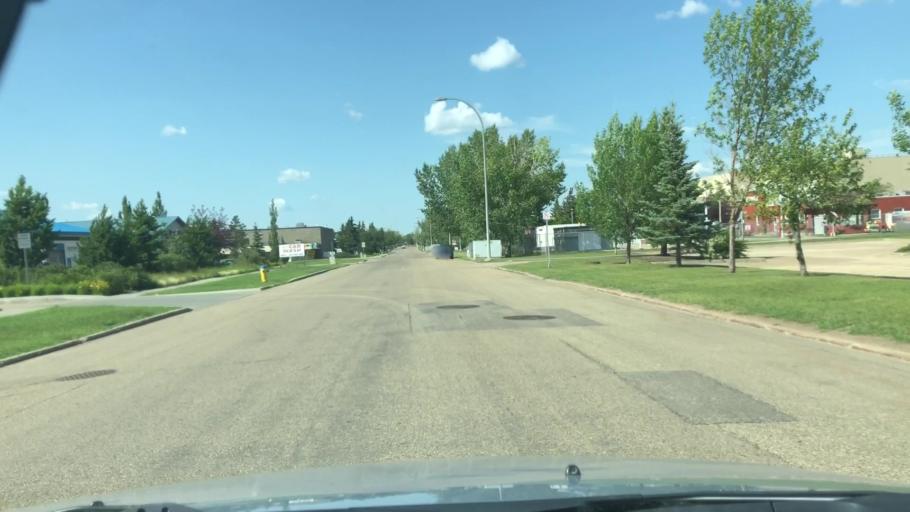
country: CA
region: Alberta
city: Edmonton
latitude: 53.5291
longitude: -113.4149
